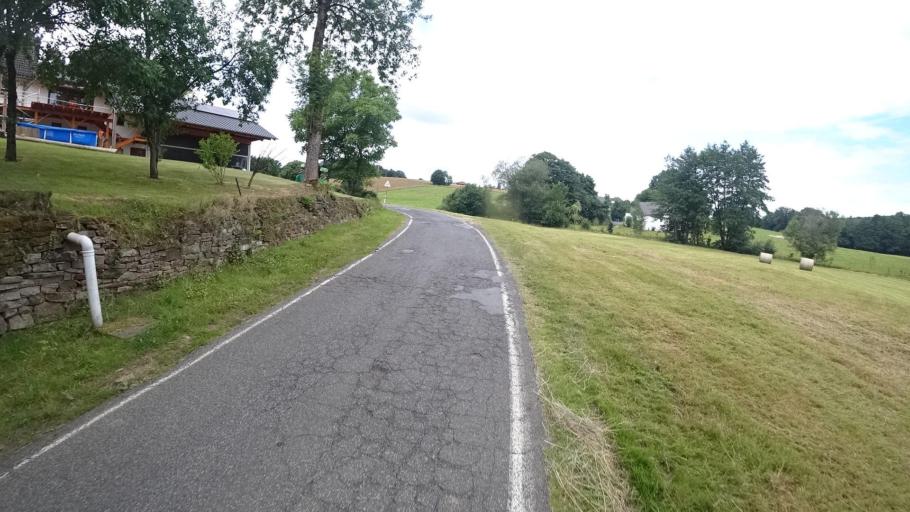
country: DE
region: Rheinland-Pfalz
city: Hirz-Maulsbach
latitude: 50.6814
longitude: 7.4900
